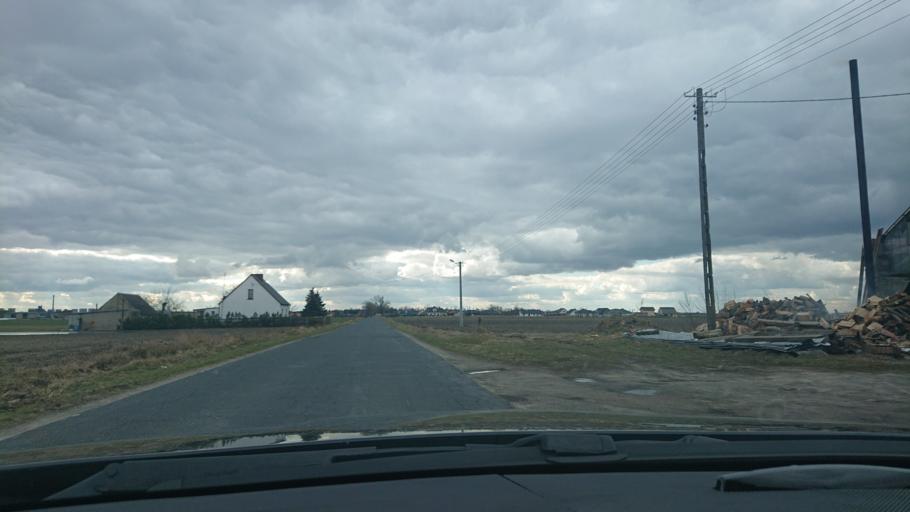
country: PL
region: Greater Poland Voivodeship
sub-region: Powiat gnieznienski
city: Gniezno
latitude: 52.5827
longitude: 17.6472
